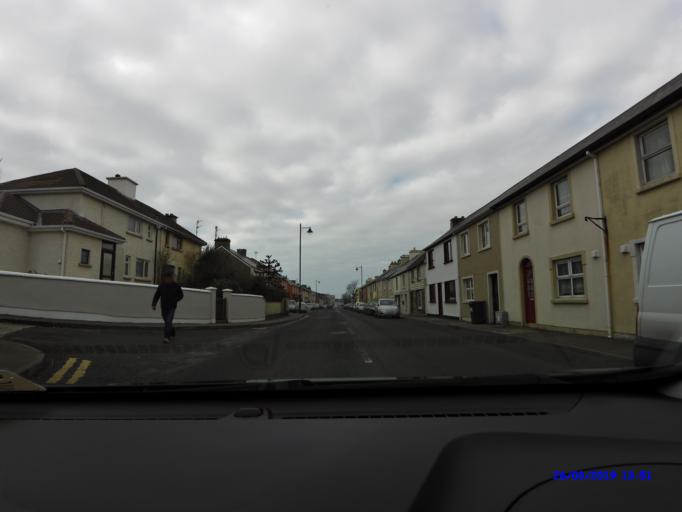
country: IE
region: Connaught
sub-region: Maigh Eo
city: Belmullet
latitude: 54.2226
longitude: -9.9834
